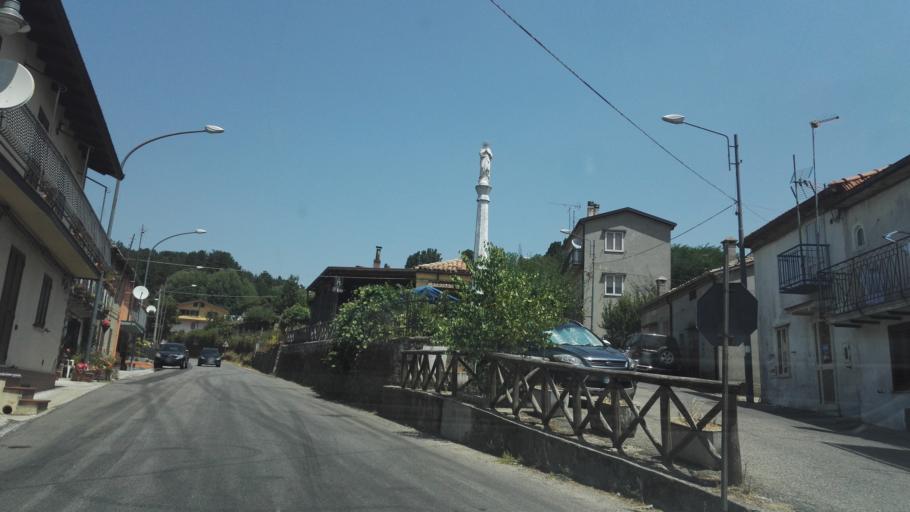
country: IT
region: Calabria
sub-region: Provincia di Vibo-Valentia
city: Mongiana
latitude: 38.5158
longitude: 16.3206
